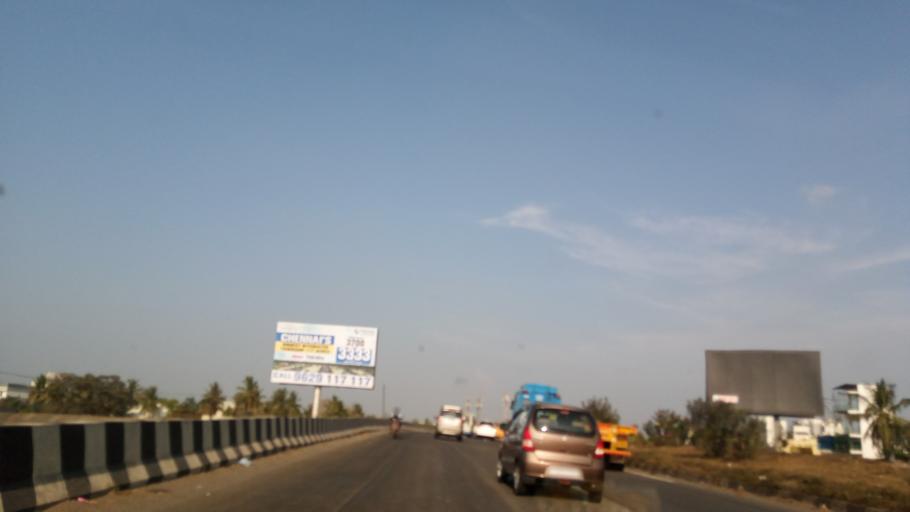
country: IN
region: Tamil Nadu
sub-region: Kancheepuram
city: Poonamalle
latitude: 13.0569
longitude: 80.1134
